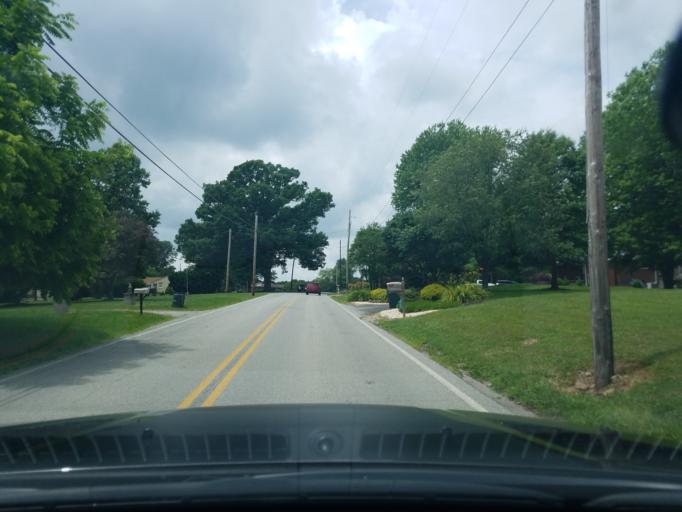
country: US
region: Pennsylvania
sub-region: Westmoreland County
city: Youngwood
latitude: 40.2199
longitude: -79.5630
